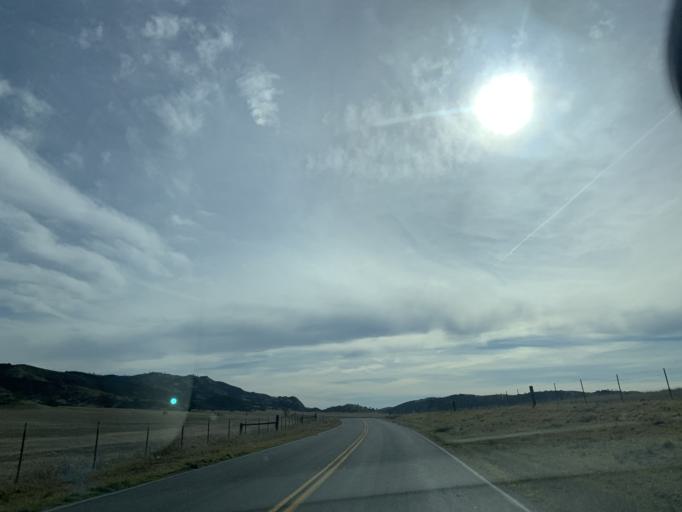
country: US
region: California
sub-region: Monterey County
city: Greenfield
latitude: 36.4893
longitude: -121.0760
